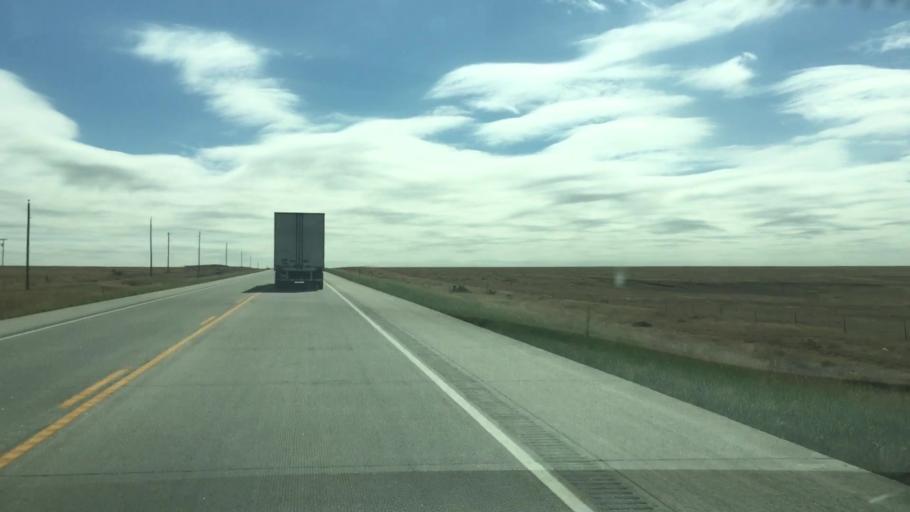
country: US
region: Colorado
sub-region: Lincoln County
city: Hugo
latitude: 39.0104
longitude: -103.2986
